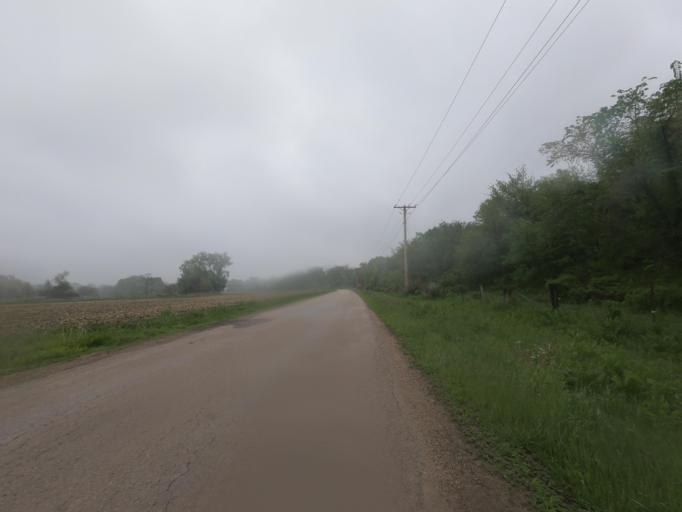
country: US
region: Wisconsin
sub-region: Grant County
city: Hazel Green
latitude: 42.5078
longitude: -90.4788
